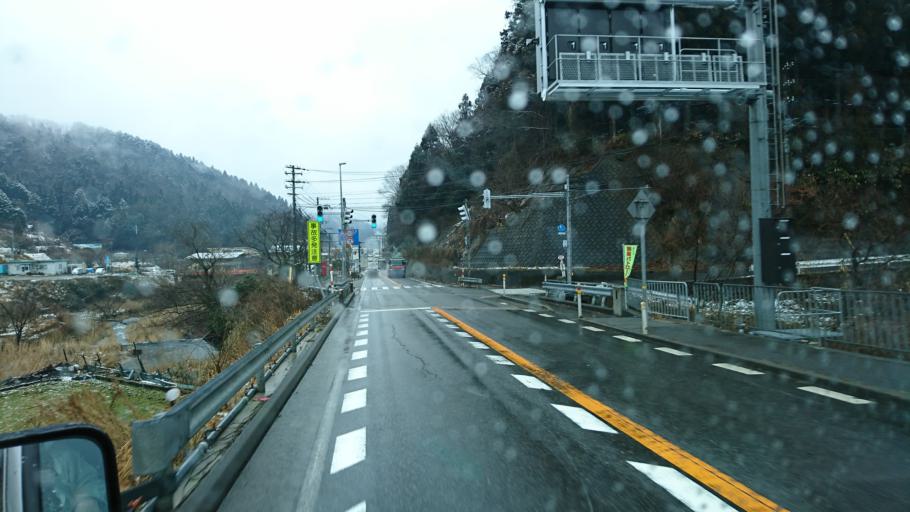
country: JP
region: Tottori
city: Tottori
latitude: 35.5492
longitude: 134.4966
